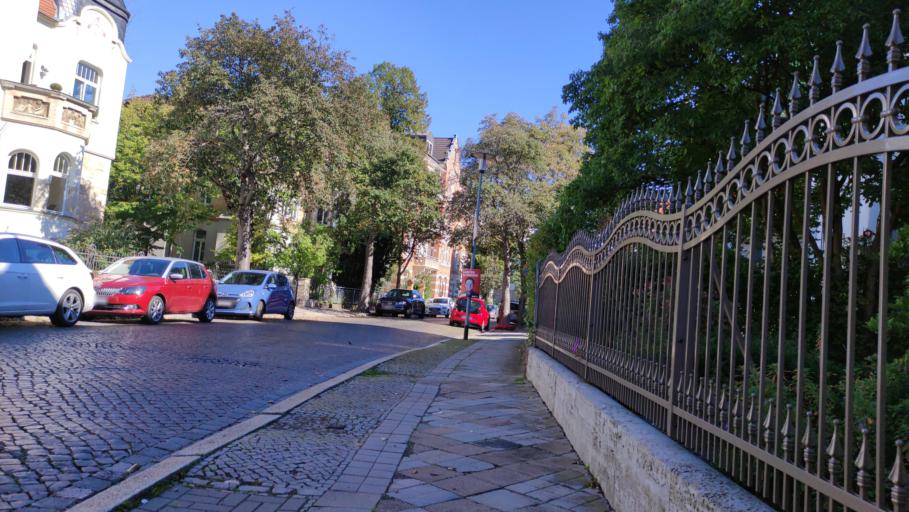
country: DE
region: Thuringia
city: Erfurt
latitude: 50.9647
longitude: 11.0232
